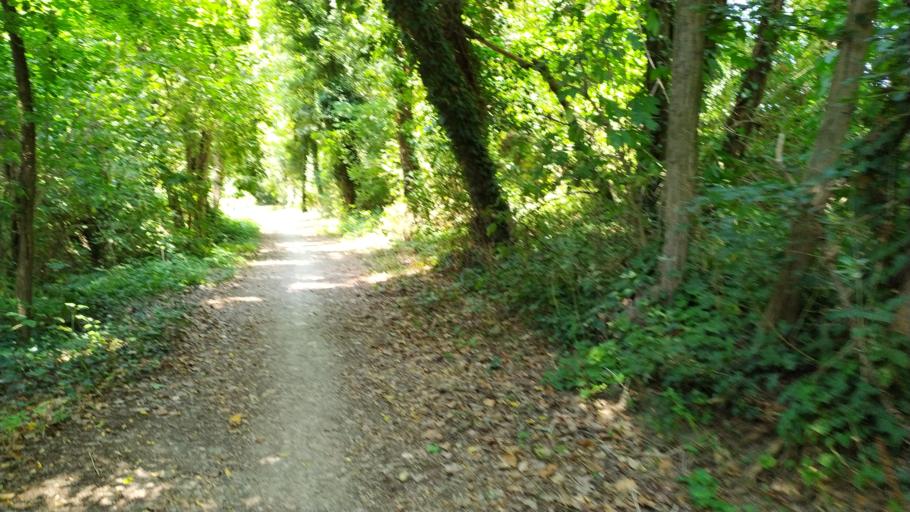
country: IT
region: Emilia-Romagna
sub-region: Forli-Cesena
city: Castrocaro Terme e Terra del Sole
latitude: 44.2003
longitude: 11.9945
